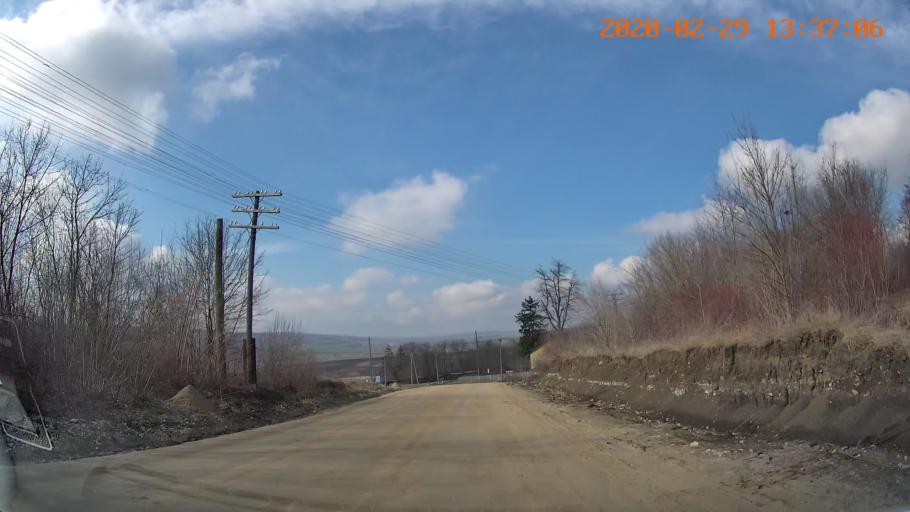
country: MD
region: Telenesti
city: Camenca
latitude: 47.8622
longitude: 28.6038
